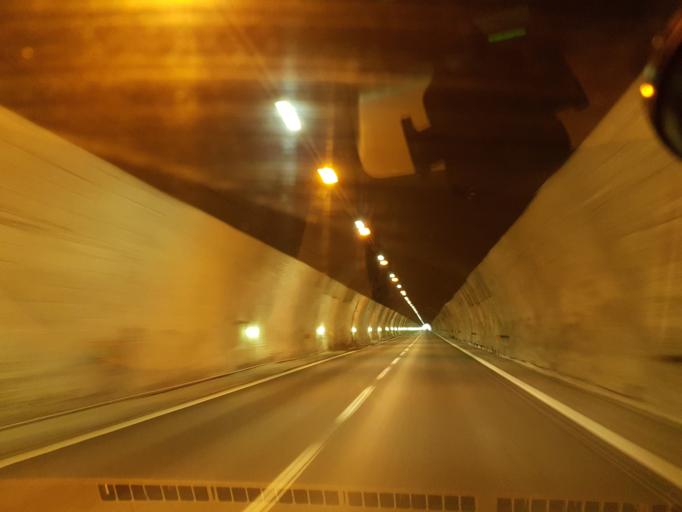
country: IT
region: Liguria
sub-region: Provincia di Genova
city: Isola del Cantone
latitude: 44.6532
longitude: 8.9544
